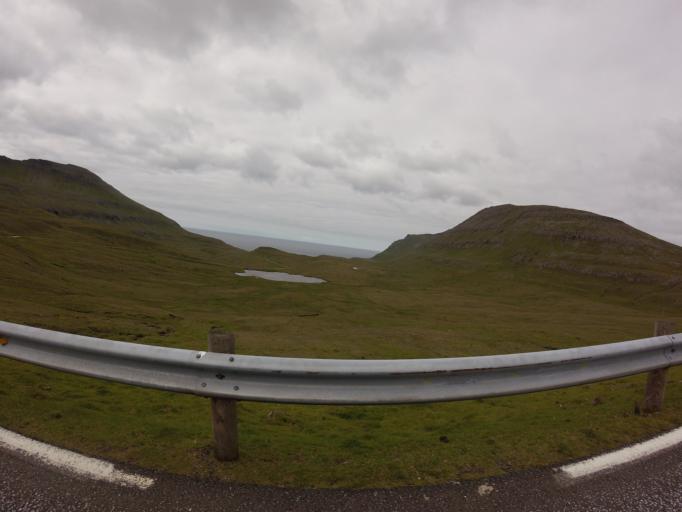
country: FO
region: Suduroy
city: Tvoroyri
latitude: 61.5175
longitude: -6.8386
